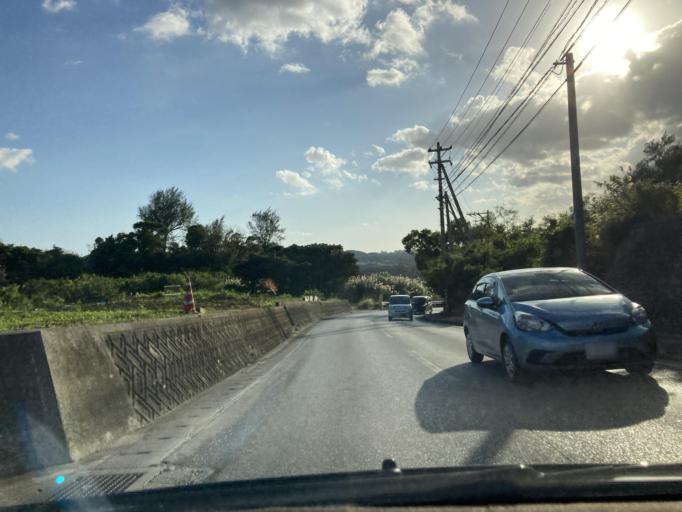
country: JP
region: Okinawa
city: Chatan
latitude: 26.2920
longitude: 127.7945
